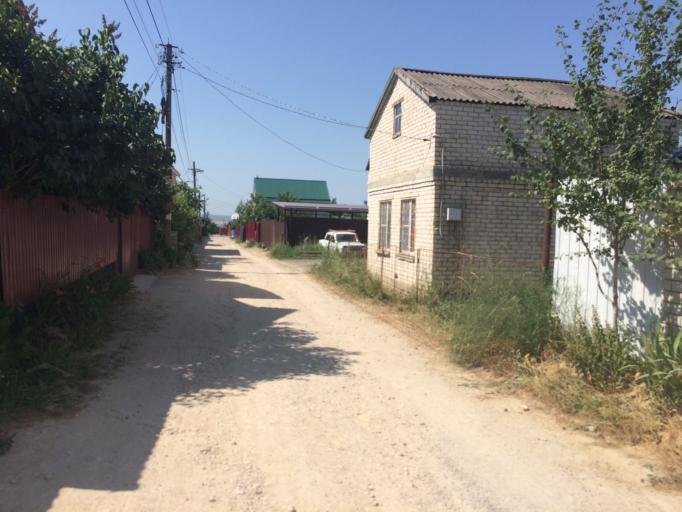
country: RU
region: Stavropol'skiy
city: Tatarka
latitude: 44.9865
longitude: 41.9422
